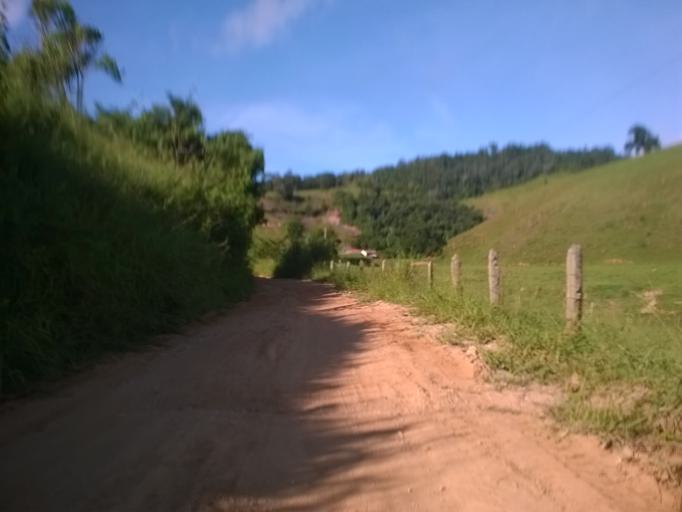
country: BR
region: Minas Gerais
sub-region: Uba
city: Uba
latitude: -21.0911
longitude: -43.0132
